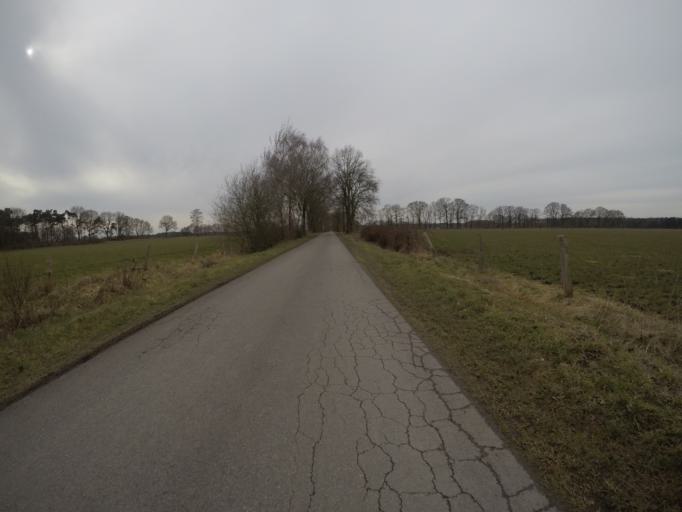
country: DE
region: North Rhine-Westphalia
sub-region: Regierungsbezirk Munster
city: Rhede
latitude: 51.7752
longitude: 6.6748
